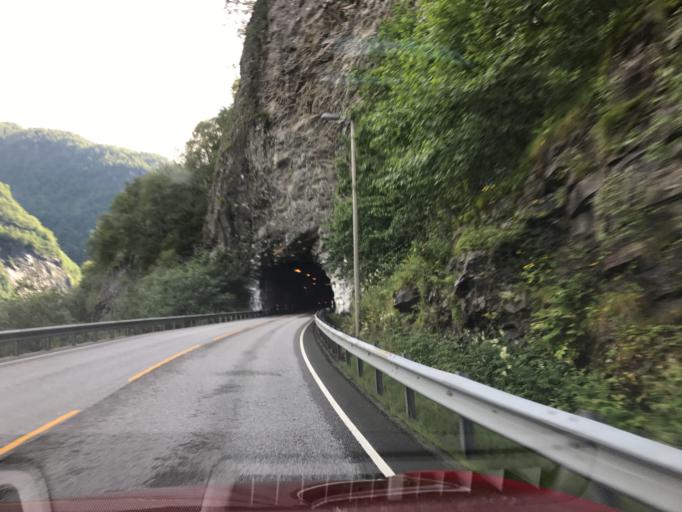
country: NO
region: Hordaland
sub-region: Vaksdal
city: Dale
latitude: 60.6469
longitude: 6.0058
